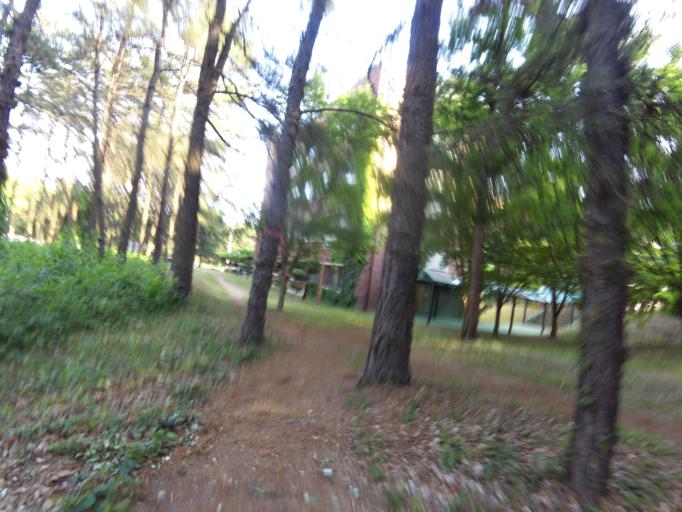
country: KR
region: Gyeongsangbuk-do
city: Gyeongsan-si
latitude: 35.8355
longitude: 128.7617
